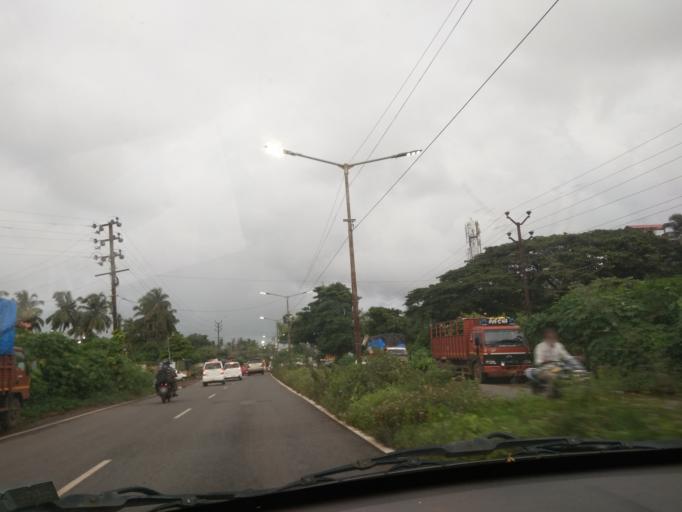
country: IN
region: Goa
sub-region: South Goa
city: Davorlim
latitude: 15.2773
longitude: 73.9808
